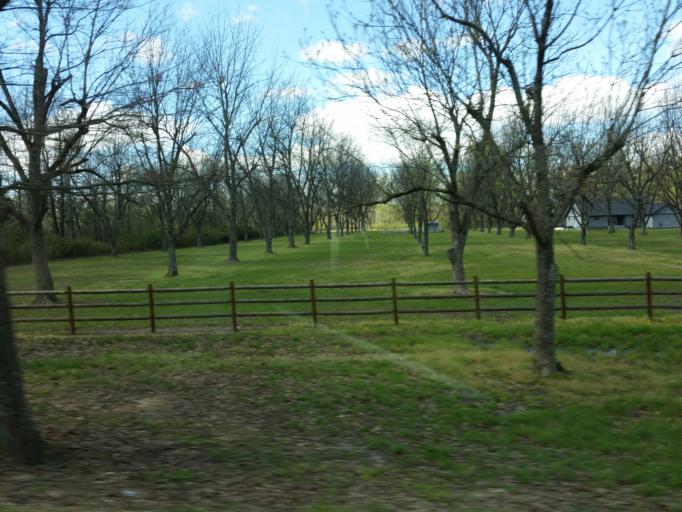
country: US
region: Arkansas
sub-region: Craighead County
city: Bono
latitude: 35.9654
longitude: -90.7146
